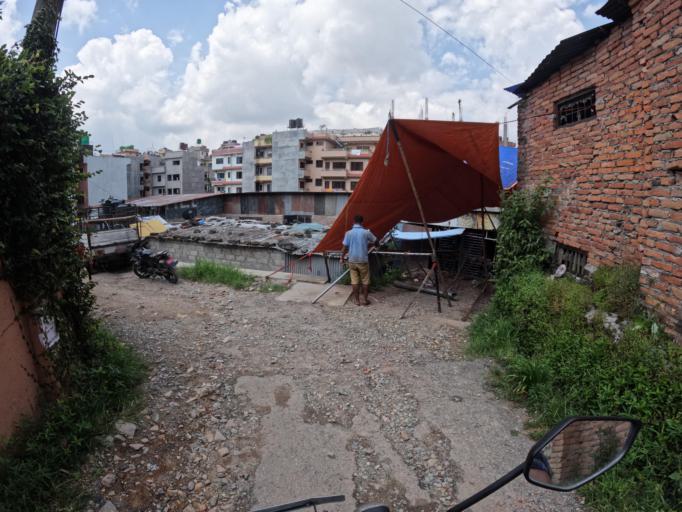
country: NP
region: Central Region
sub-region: Bagmati Zone
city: Patan
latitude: 27.6734
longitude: 85.3618
